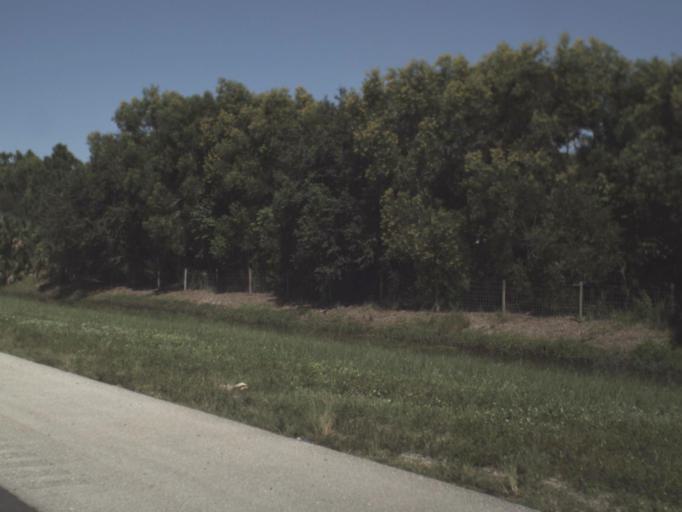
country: US
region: Florida
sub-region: Lee County
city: Bonita Springs
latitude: 26.3422
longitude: -81.7523
